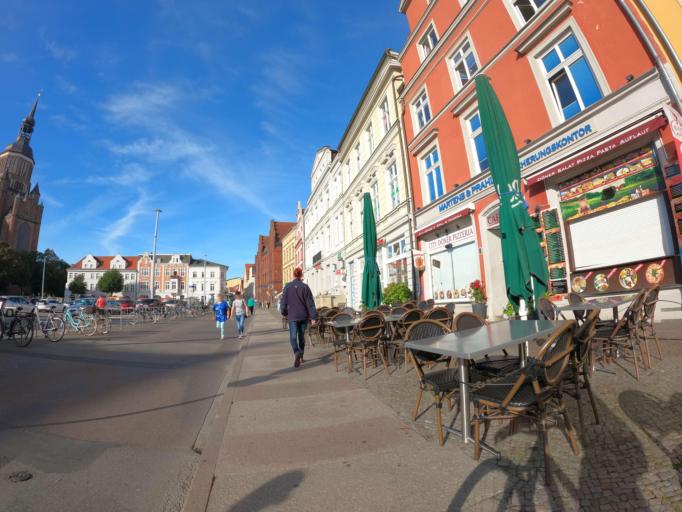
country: DE
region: Mecklenburg-Vorpommern
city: Stralsund
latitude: 54.3114
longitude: 13.0881
